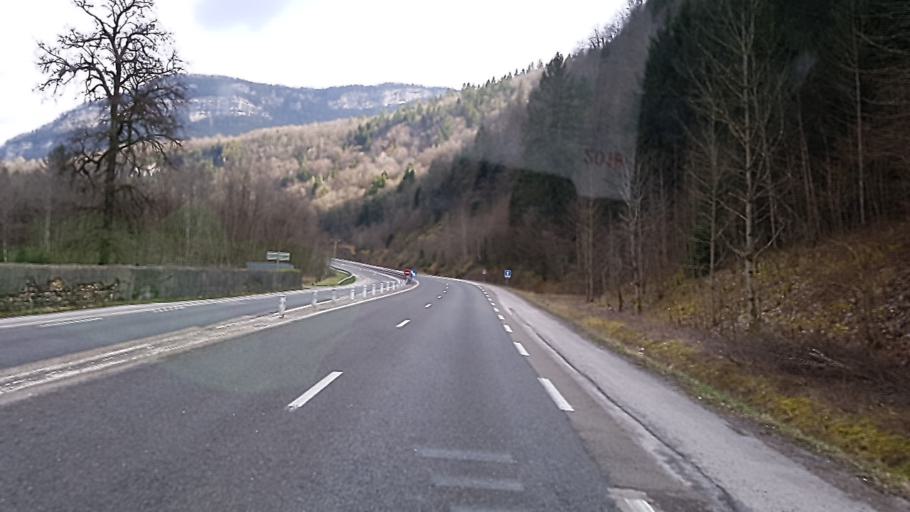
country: FR
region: Franche-Comte
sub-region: Departement du Jura
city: Saint-Lupicin
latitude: 46.3790
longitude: 5.8086
